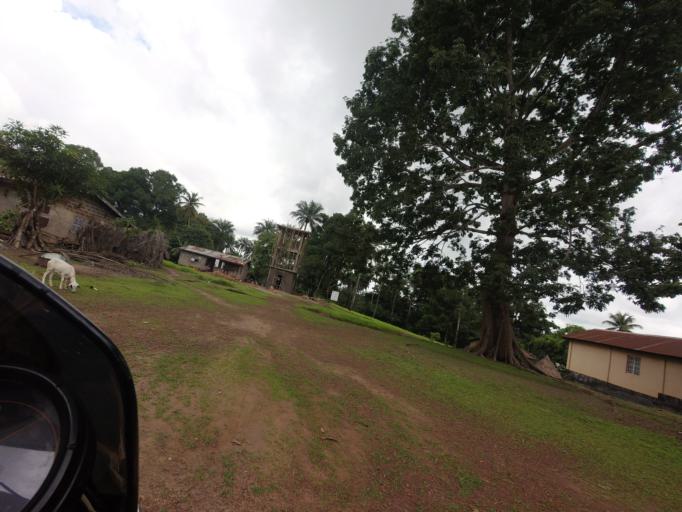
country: SL
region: Northern Province
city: Mambolo
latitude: 8.9720
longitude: -12.9981
